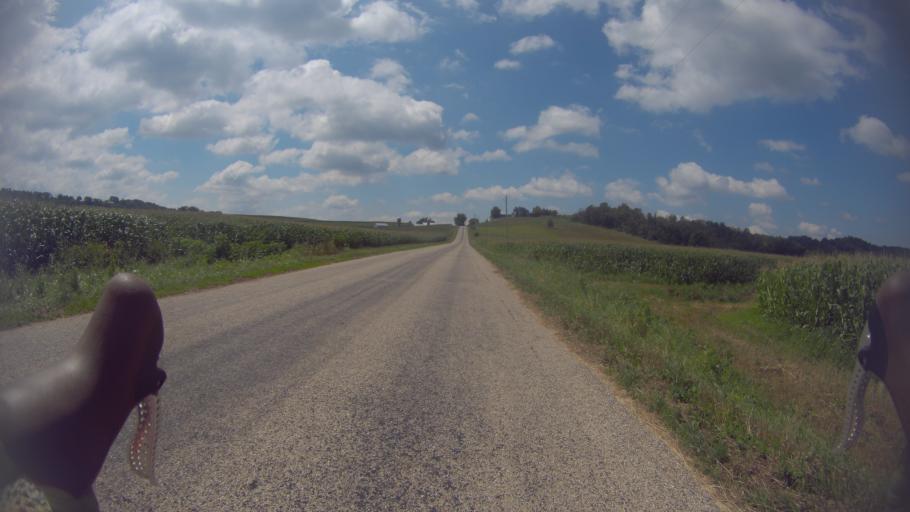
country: US
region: Wisconsin
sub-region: Sauk County
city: Sauk City
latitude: 43.2391
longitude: -89.6374
